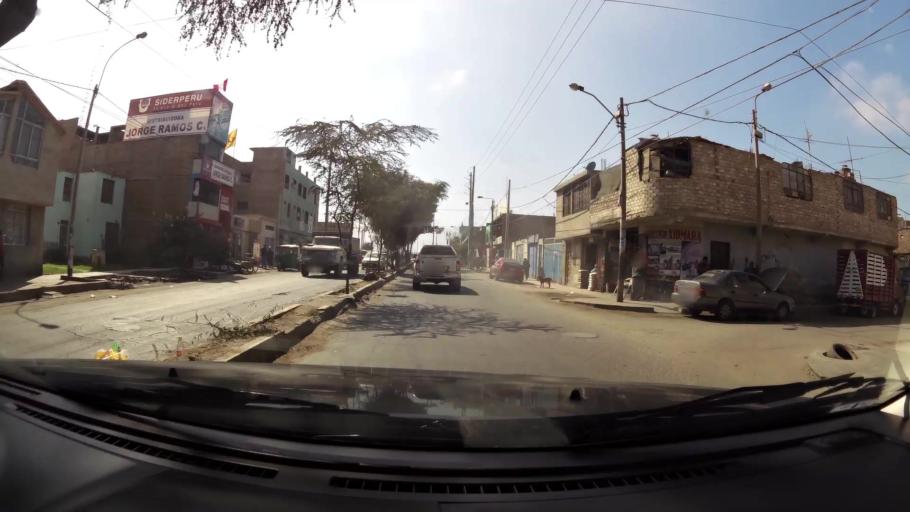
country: PE
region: Ica
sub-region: Provincia de Ica
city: Ica
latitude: -14.0709
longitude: -75.7220
